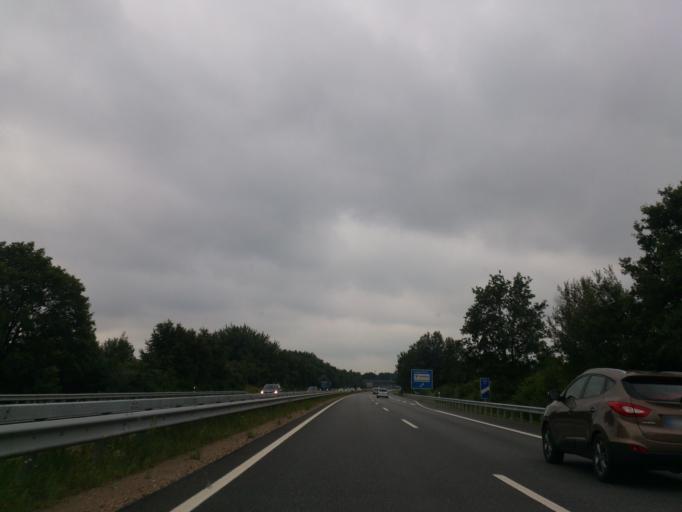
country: DE
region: Schleswig-Holstein
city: Ottenbuttel
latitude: 53.9629
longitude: 9.4917
